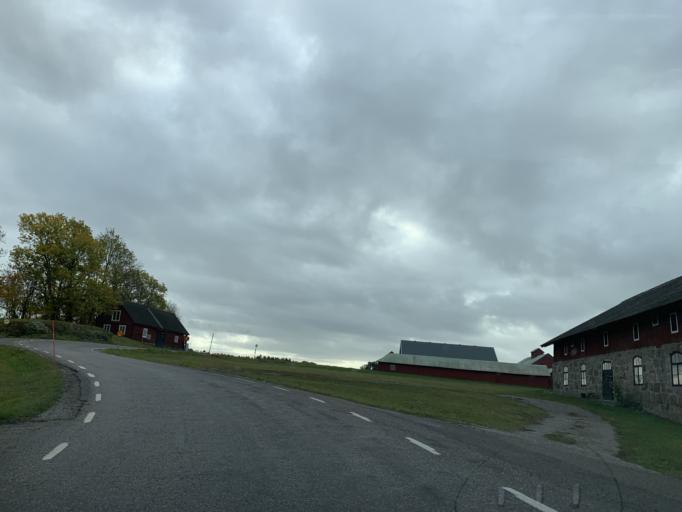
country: SE
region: Stockholm
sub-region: Nynashamns Kommun
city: Osmo
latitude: 58.9584
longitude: 17.7658
